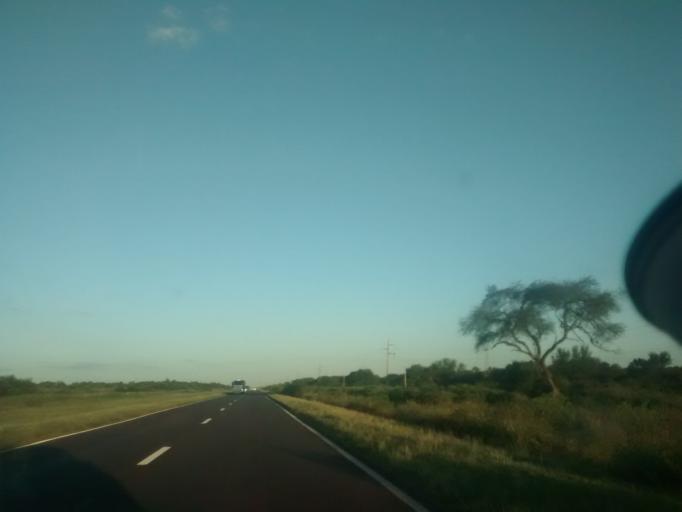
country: AR
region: Chaco
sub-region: Departamento de Presidencia de la Plaza
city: Presidencia de la Plaza
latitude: -27.0806
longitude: -59.6610
